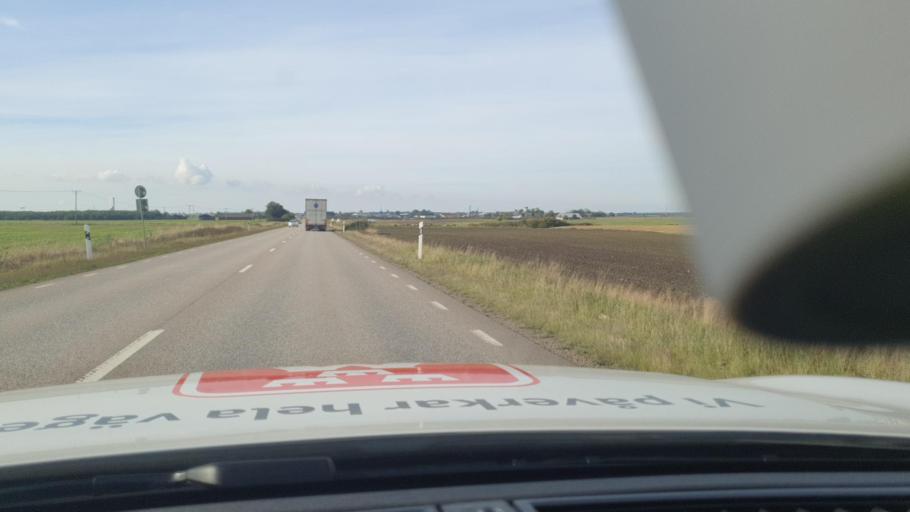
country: SE
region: Skane
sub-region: Angelholms Kommun
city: Munka-Ljungby
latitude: 56.2537
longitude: 12.9369
